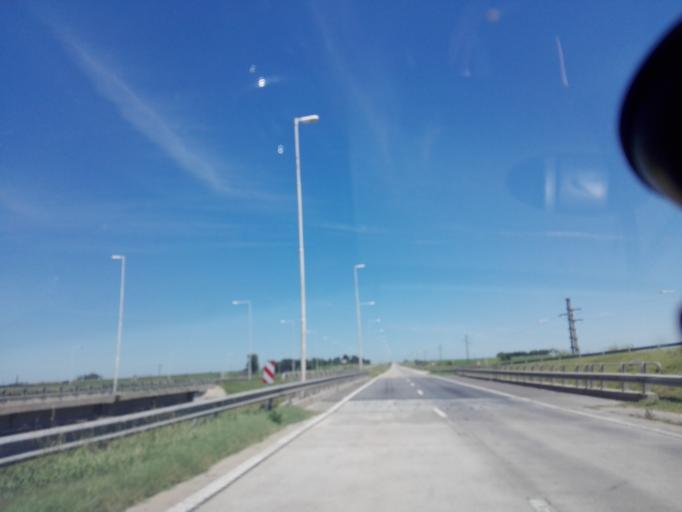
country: AR
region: Santa Fe
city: Canada de Gomez
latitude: -32.8462
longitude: -61.3920
